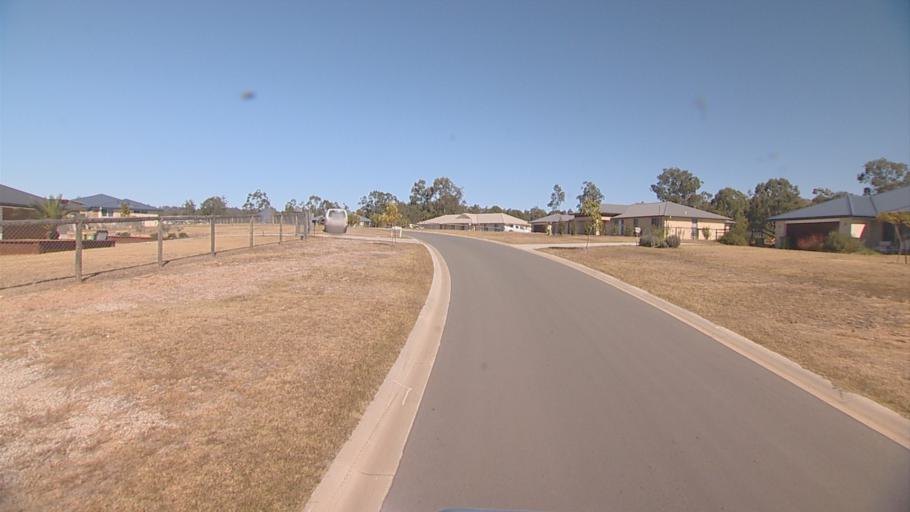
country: AU
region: Queensland
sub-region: Logan
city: Cedar Vale
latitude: -27.8666
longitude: 153.0426
